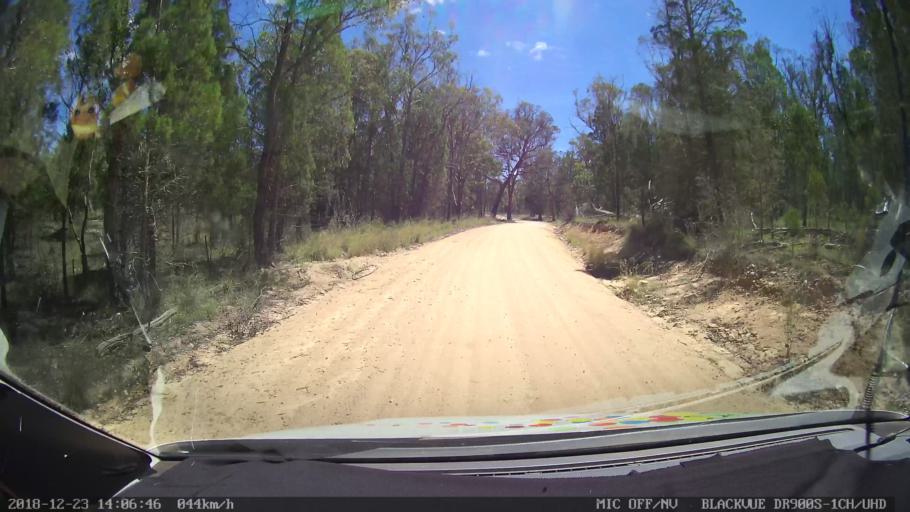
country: AU
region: New South Wales
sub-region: Tamworth Municipality
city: Manilla
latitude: -30.6319
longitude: 151.0744
